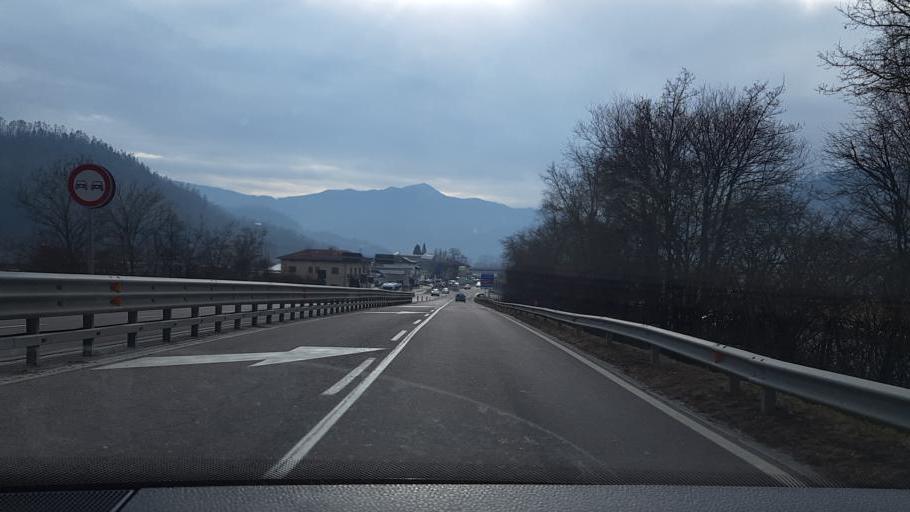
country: IT
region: Trentino-Alto Adige
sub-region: Provincia di Trento
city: Pergine Valsugana
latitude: 46.0508
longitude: 11.2346
